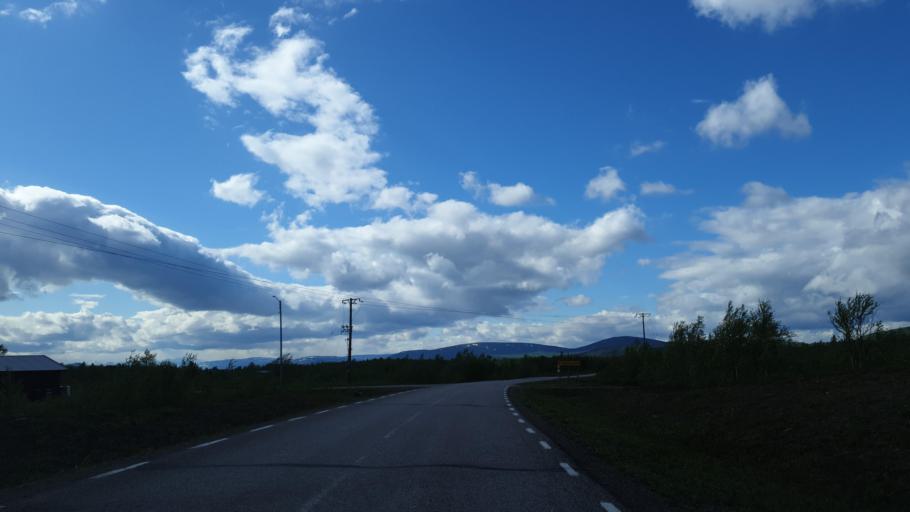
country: SE
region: Norrbotten
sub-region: Kiruna Kommun
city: Kiruna
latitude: 67.7675
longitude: 19.9826
